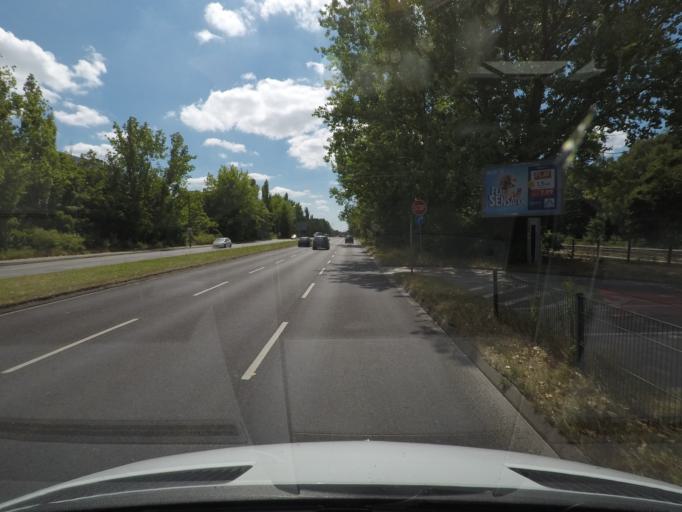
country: DE
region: Berlin
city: Falkenberg
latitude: 52.5500
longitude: 13.5474
